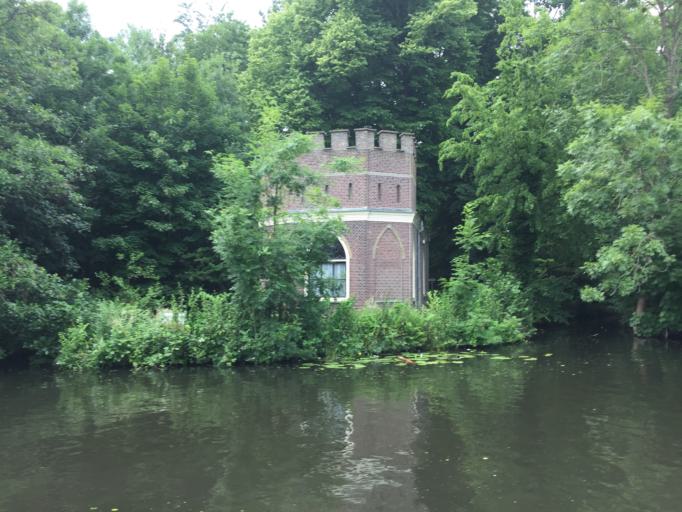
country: NL
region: South Holland
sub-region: Gemeente Oegstgeest
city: Oegstgeest
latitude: 52.1792
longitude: 4.4873
